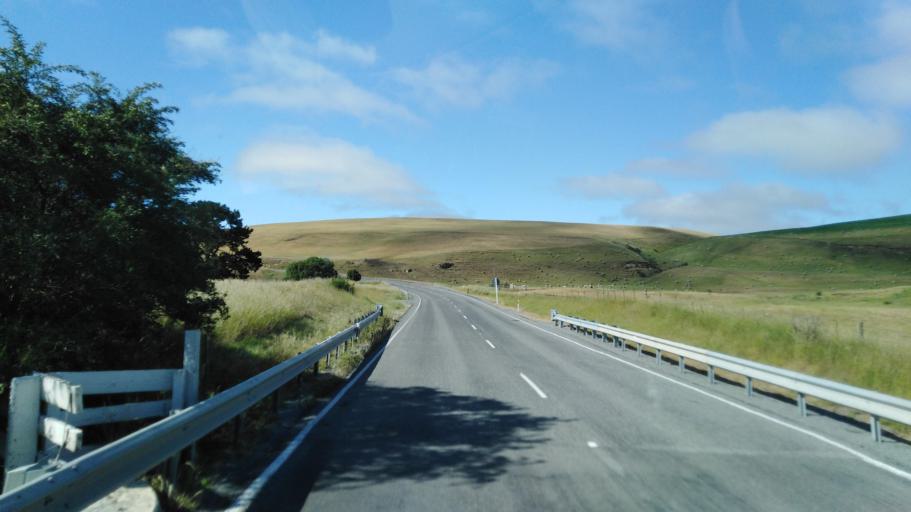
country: NZ
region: Canterbury
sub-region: Hurunui District
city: Amberley
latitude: -43.0223
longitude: 172.7087
